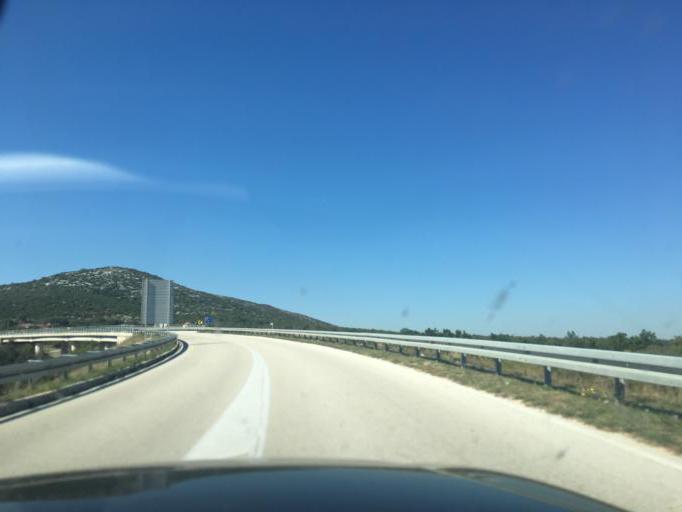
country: HR
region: Splitsko-Dalmatinska
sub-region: Grad Trogir
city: Trogir
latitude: 43.6129
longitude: 16.2272
